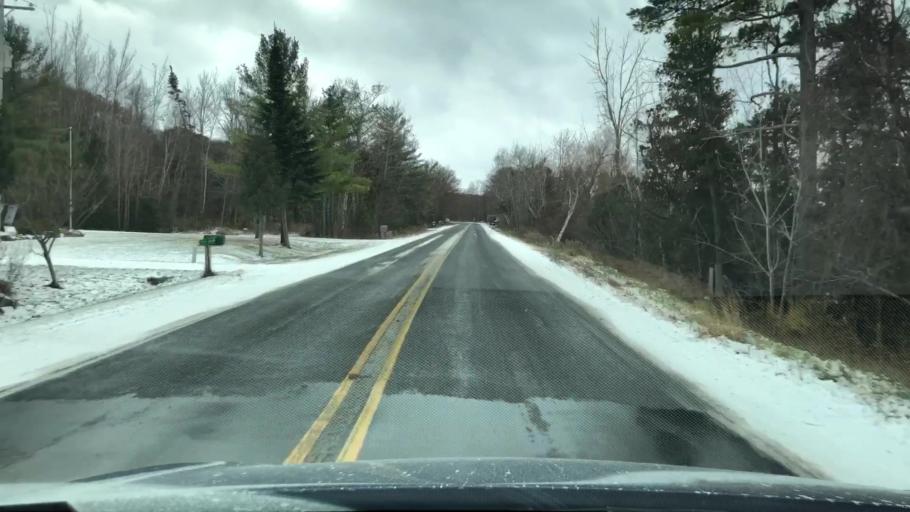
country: US
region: Michigan
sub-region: Leelanau County
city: Greilickville
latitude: 44.8358
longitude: -85.5620
